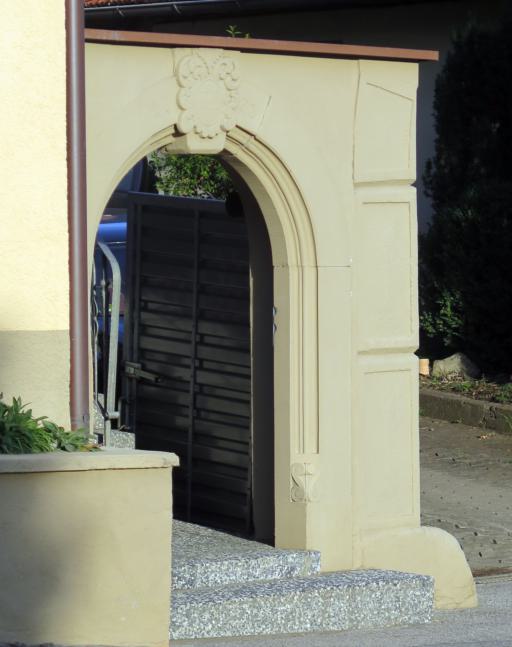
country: DE
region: Bavaria
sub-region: Regierungsbezirk Unterfranken
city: Hassfurt
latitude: 50.0584
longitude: 10.5234
